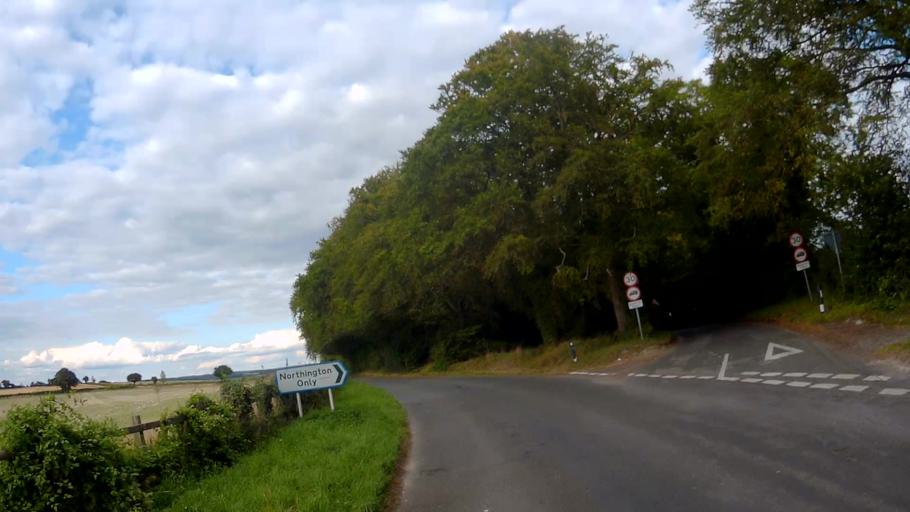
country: GB
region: England
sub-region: Hampshire
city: Kings Worthy
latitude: 51.1348
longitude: -1.1991
